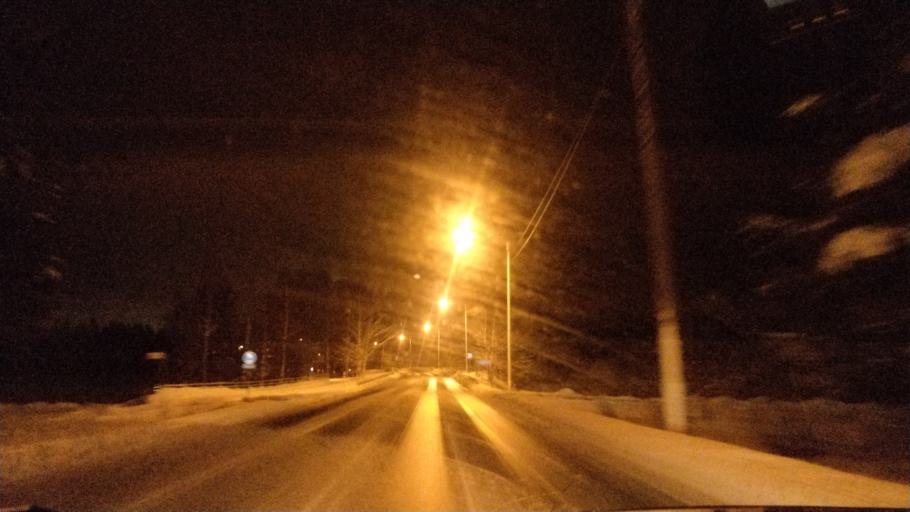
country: FI
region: Lapland
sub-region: Rovaniemi
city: Rovaniemi
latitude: 66.3933
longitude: 25.3812
